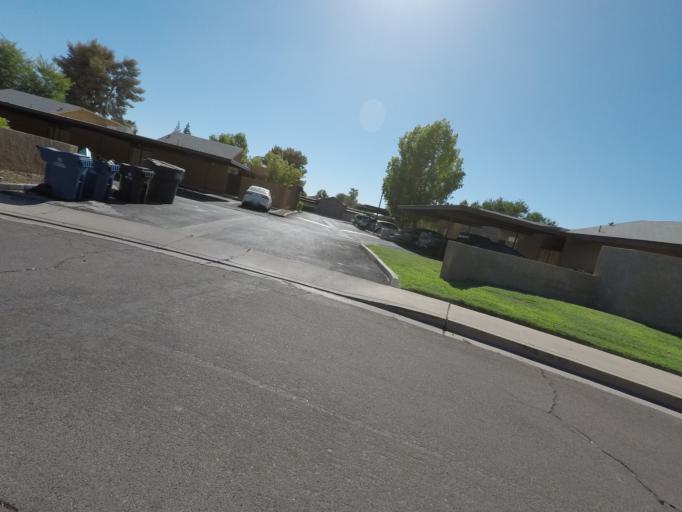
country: US
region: Arizona
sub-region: Maricopa County
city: Tempe
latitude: 33.4210
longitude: -111.9056
